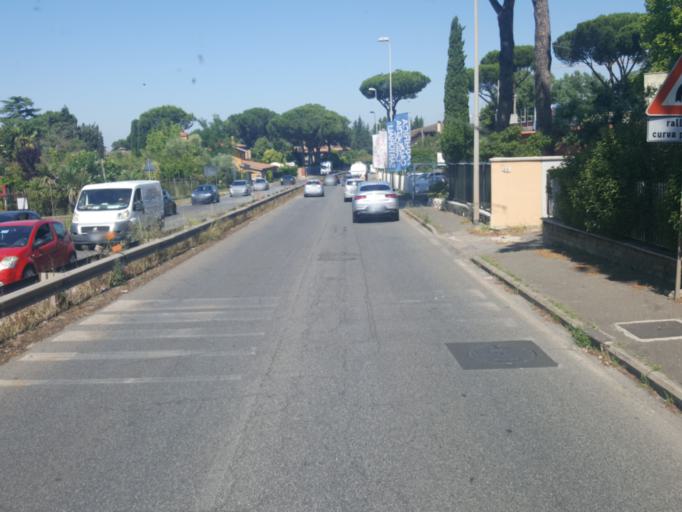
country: IT
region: Latium
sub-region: Citta metropolitana di Roma Capitale
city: Frascati
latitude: 41.8235
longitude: 12.6349
